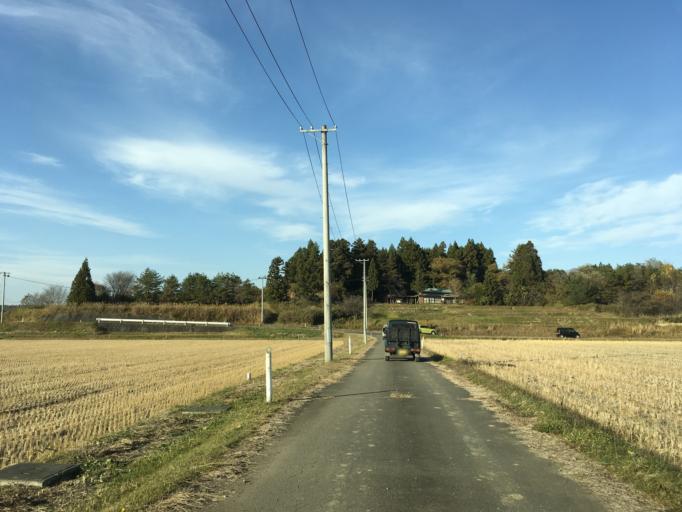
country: JP
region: Iwate
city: Ichinoseki
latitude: 38.7954
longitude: 141.1844
